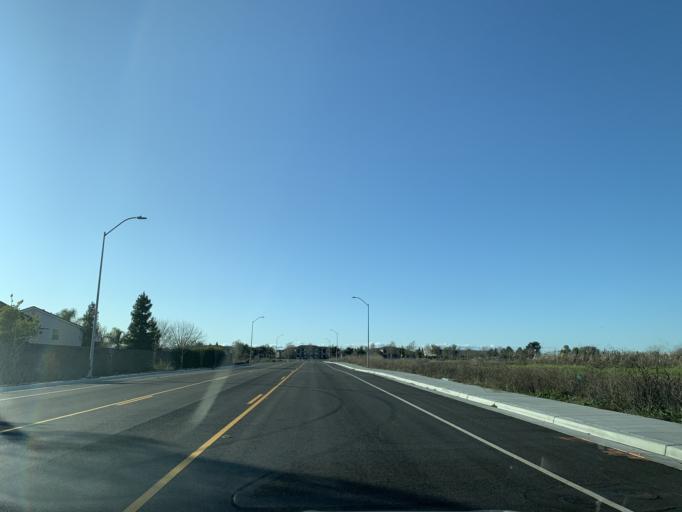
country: US
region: California
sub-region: Yolo County
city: West Sacramento
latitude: 38.5440
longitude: -121.5646
